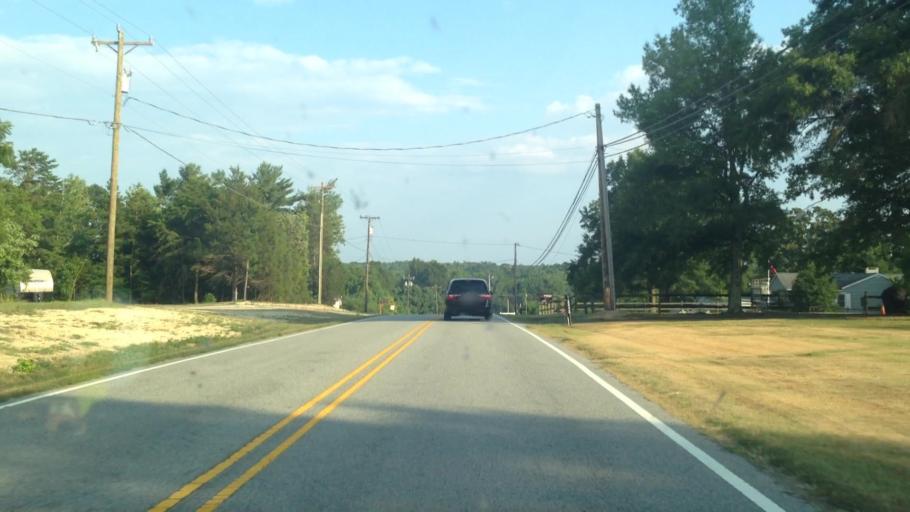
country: US
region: North Carolina
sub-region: Guilford County
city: High Point
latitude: 35.9549
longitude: -80.0722
